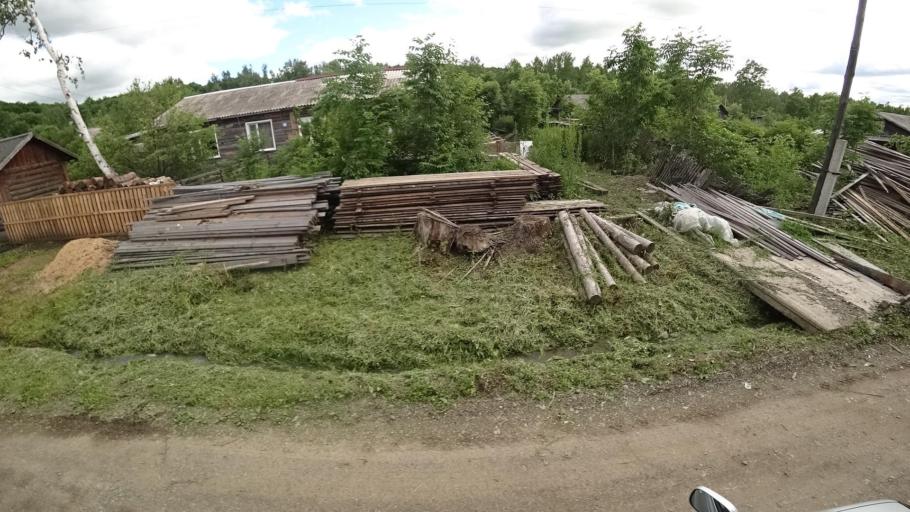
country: RU
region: Khabarovsk Krai
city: Litovko
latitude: 49.3634
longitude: 135.1712
